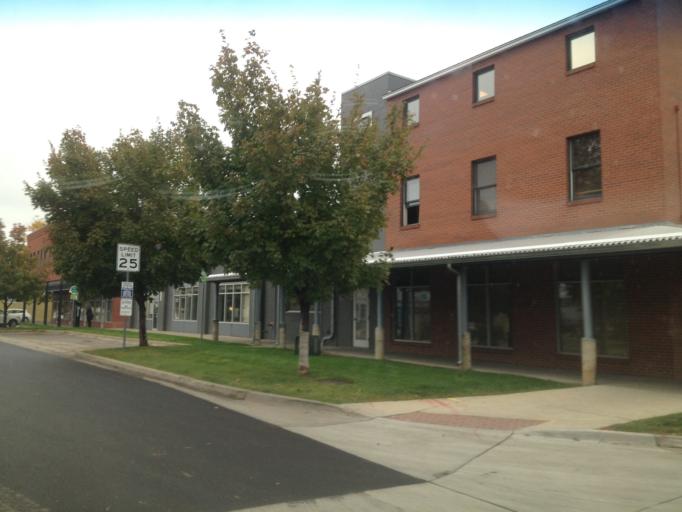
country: US
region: Colorado
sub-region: Boulder County
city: Boulder
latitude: 40.0276
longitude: -105.2537
